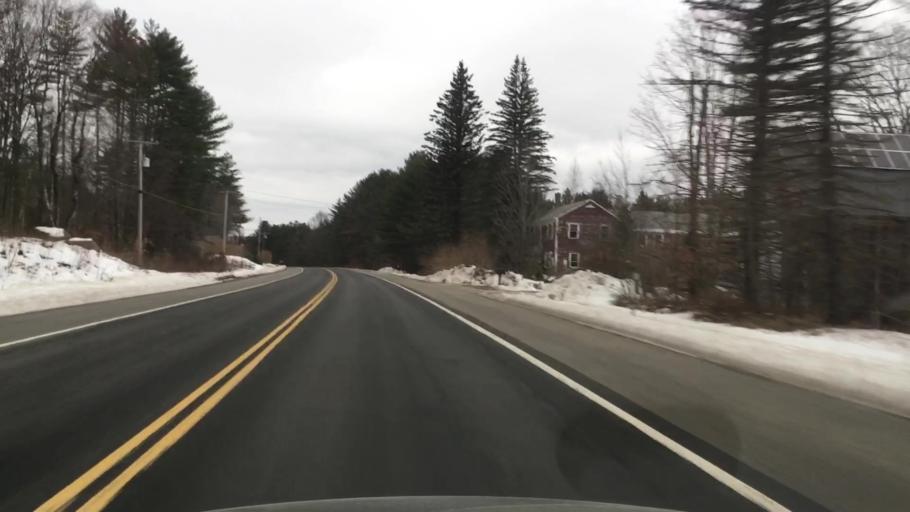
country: US
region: New Hampshire
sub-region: Merrimack County
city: Henniker
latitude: 43.2236
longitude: -71.8840
